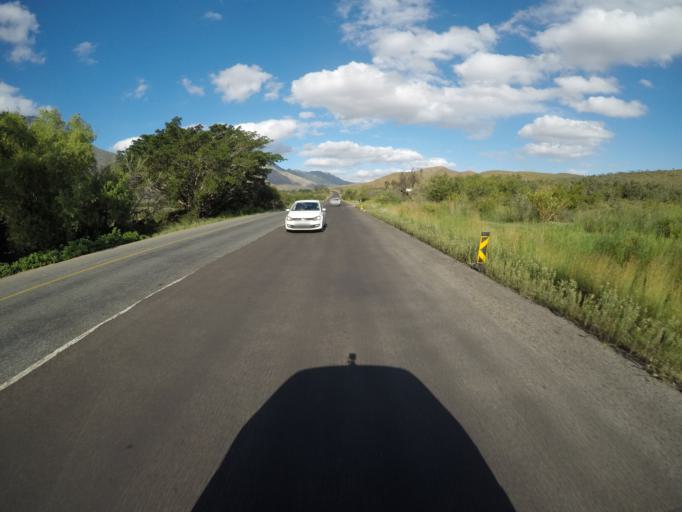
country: ZA
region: Western Cape
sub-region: Cape Winelands District Municipality
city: Ashton
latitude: -33.8685
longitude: 20.1345
